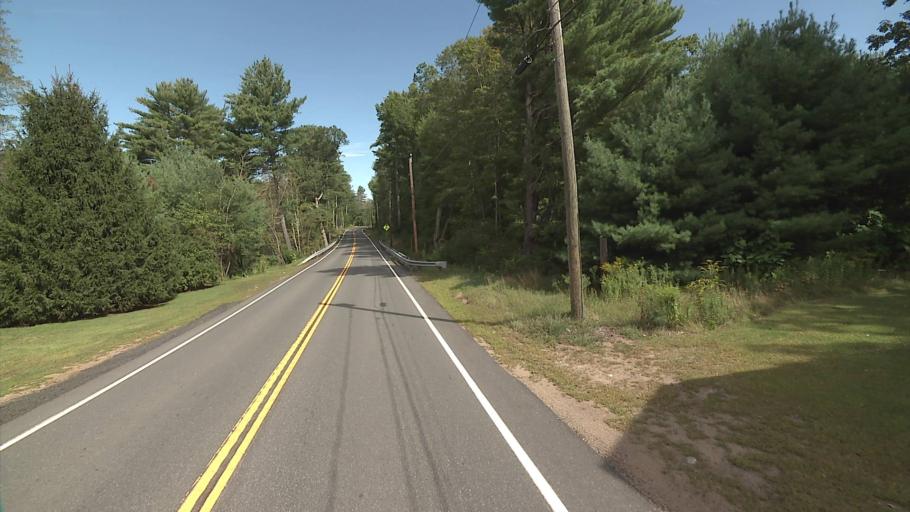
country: US
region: Connecticut
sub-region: Tolland County
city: Stafford
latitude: 42.0178
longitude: -72.3175
